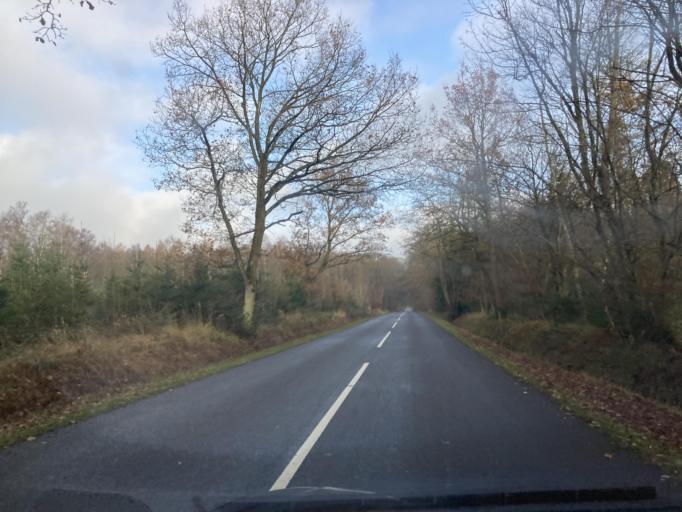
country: DK
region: Zealand
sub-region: Lolland Kommune
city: Rodby
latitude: 54.7773
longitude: 11.3683
